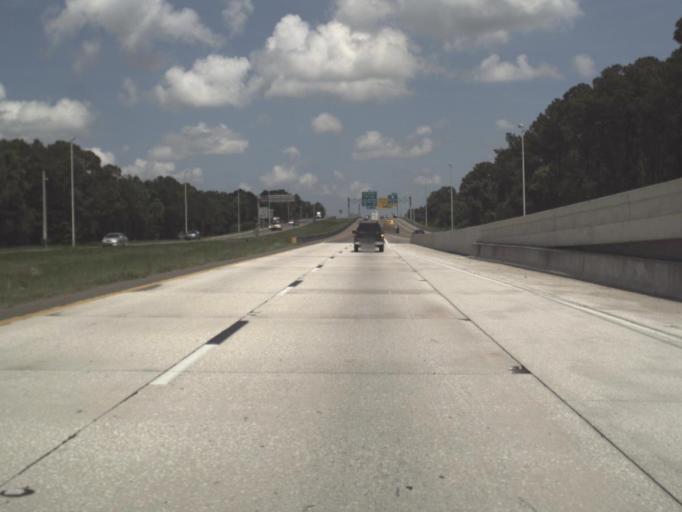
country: US
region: Florida
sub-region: Duval County
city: Jacksonville
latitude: 30.4586
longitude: -81.6431
